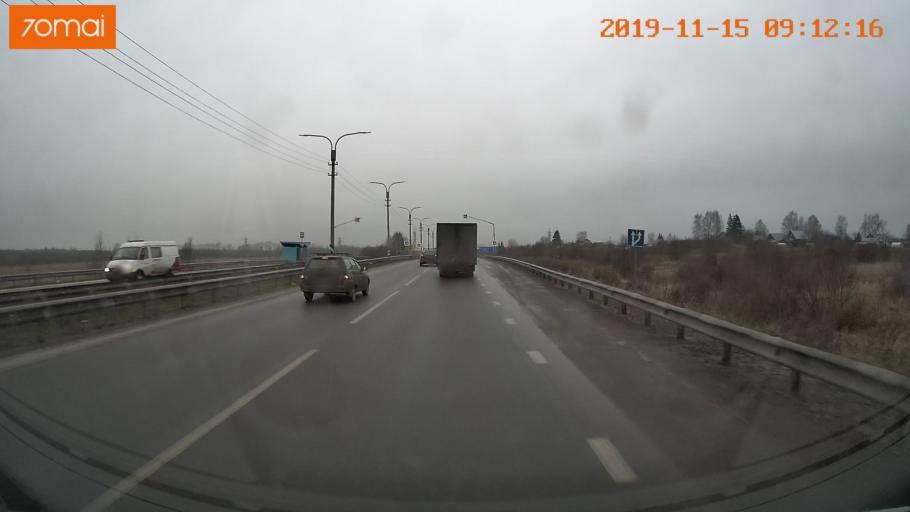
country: RU
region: Vologda
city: Tonshalovo
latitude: 59.2063
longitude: 37.9388
